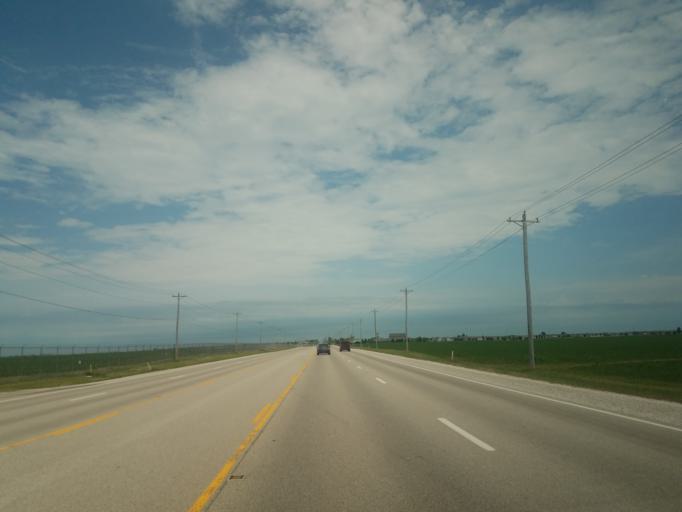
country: US
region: Illinois
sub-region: McLean County
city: Downs
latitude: 40.4791
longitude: -88.9023
